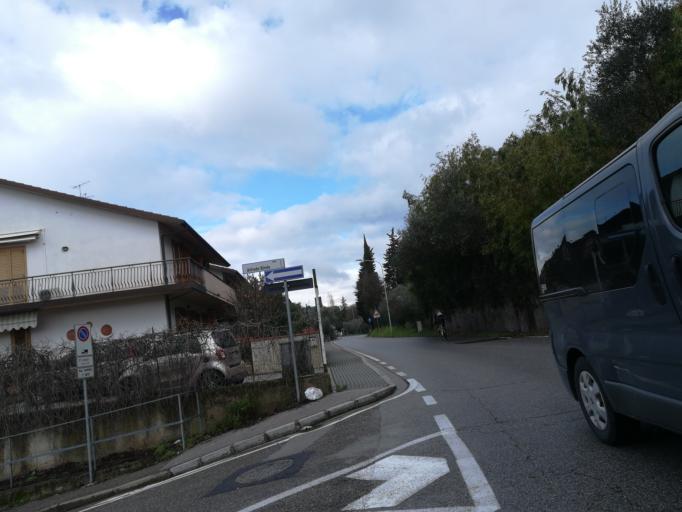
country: IT
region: Tuscany
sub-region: Provincia di Prato
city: Carmignano
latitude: 43.8011
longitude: 11.0321
